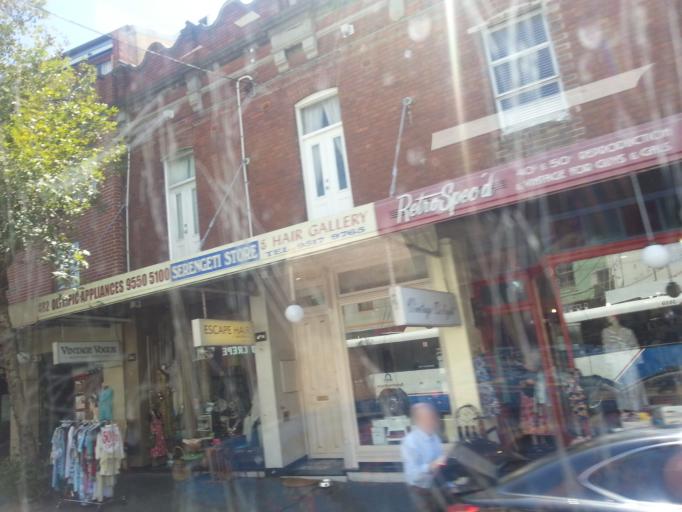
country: AU
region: New South Wales
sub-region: Marrickville
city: Newtown
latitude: -33.9017
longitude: 151.1788
